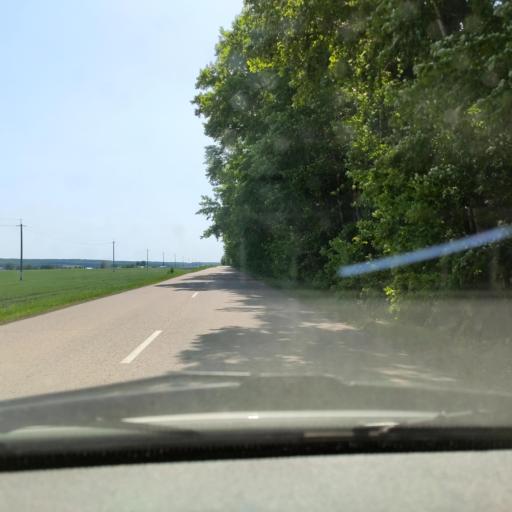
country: RU
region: Bashkortostan
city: Avdon
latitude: 54.5123
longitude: 55.6261
